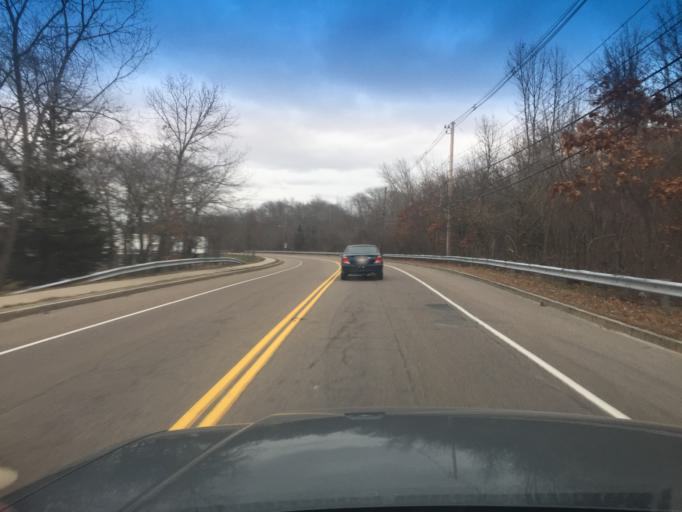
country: US
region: Massachusetts
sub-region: Norfolk County
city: Norwood
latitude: 42.1988
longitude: -71.1699
